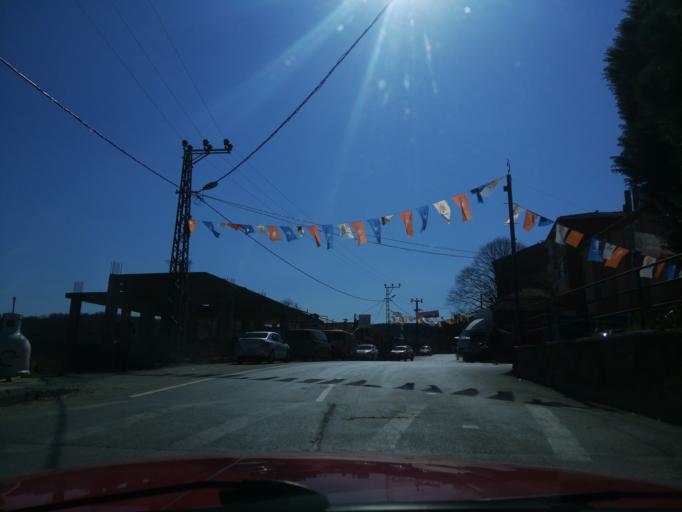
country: TR
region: Istanbul
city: Mahmut Sevket Pasa
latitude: 41.1278
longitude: 29.1597
